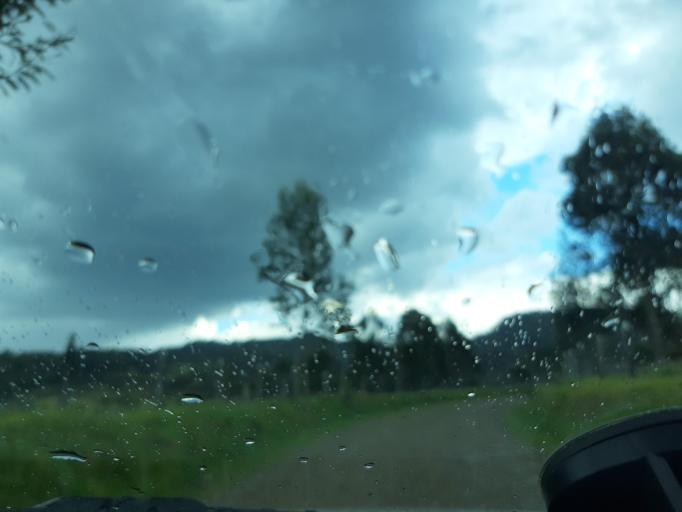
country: CO
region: Boyaca
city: Raquira
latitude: 5.4926
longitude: -73.6981
